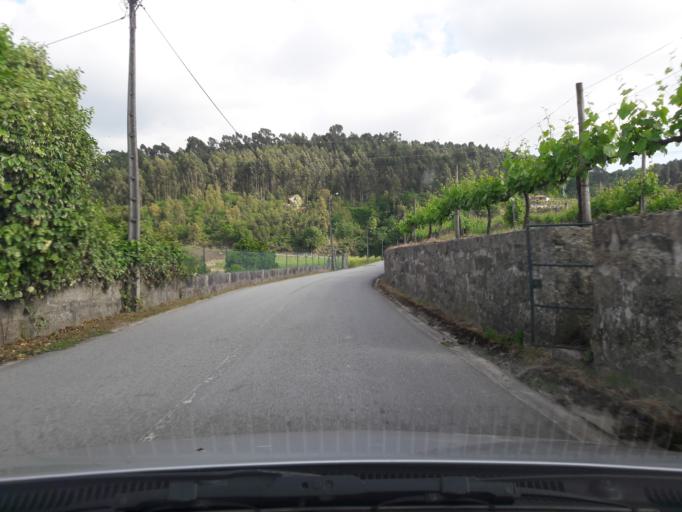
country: PT
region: Braga
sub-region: Guimaraes
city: Candoso
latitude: 41.4220
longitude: -8.3325
